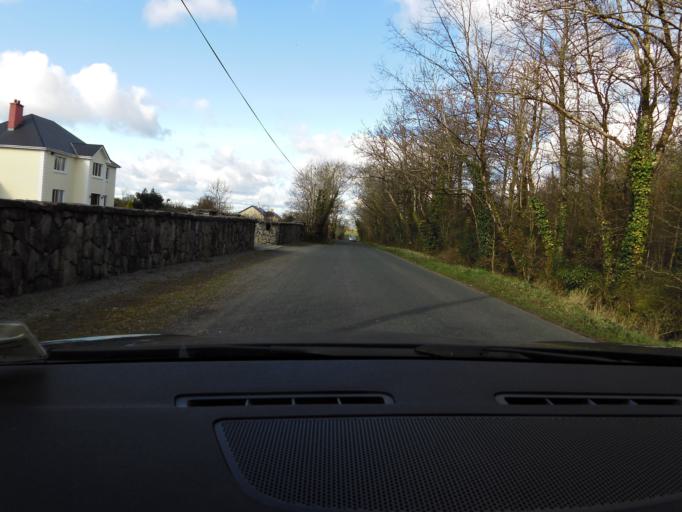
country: IE
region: Connaught
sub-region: County Galway
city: Athenry
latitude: 53.4607
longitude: -8.5492
